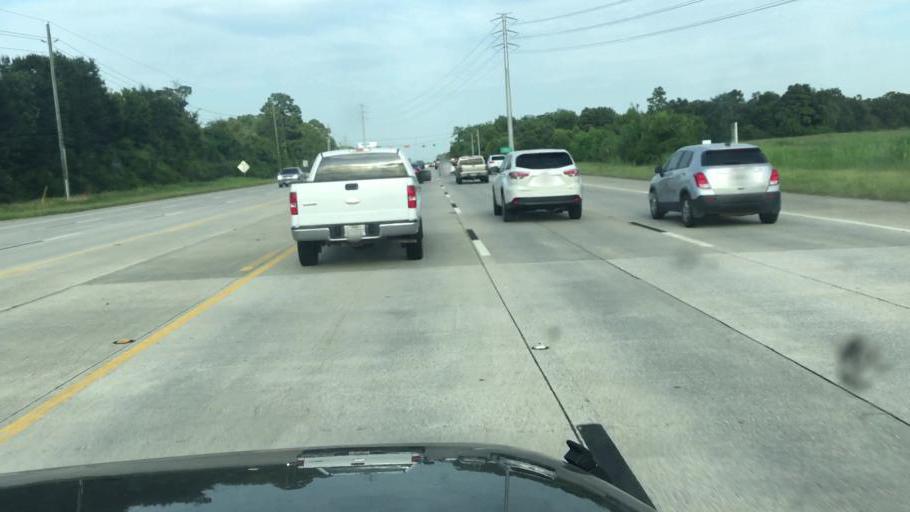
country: US
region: Texas
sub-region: Harris County
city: Spring
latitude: 30.0168
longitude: -95.3606
